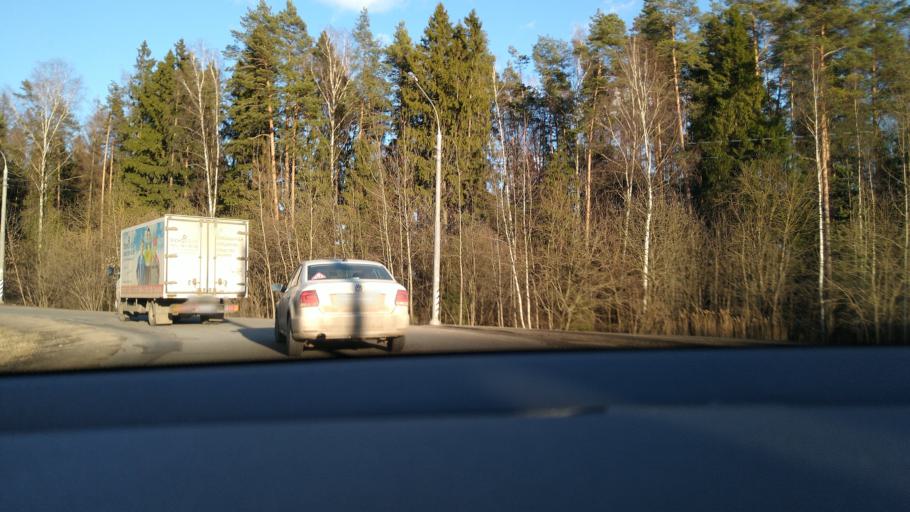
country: RU
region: Moskovskaya
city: Petrovo-Dal'neye
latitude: 55.7775
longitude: 37.1646
